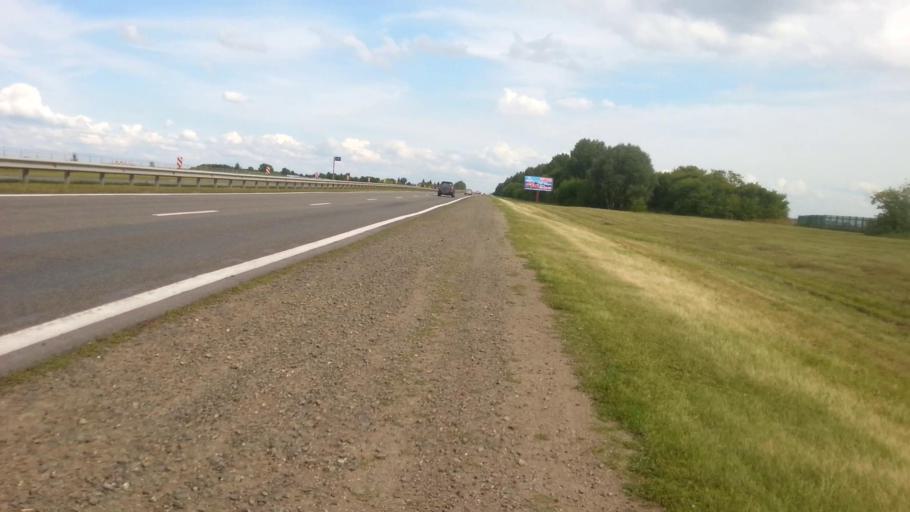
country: RU
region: Altai Krai
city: Nauchnyy Gorodok
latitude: 53.3561
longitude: 83.5148
